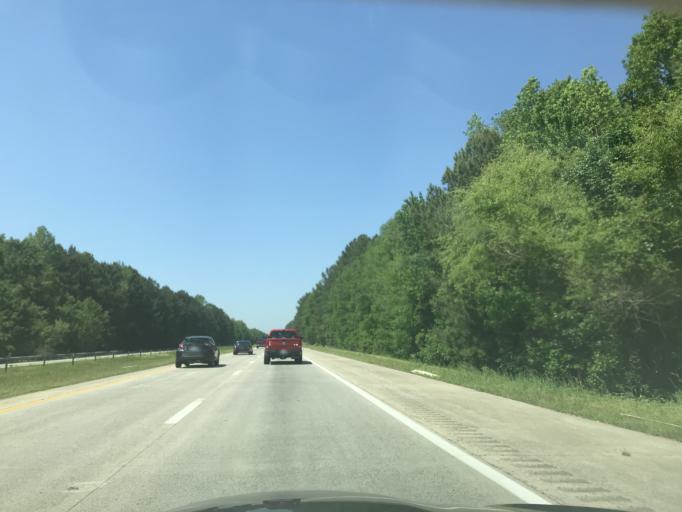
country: US
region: North Carolina
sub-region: Johnston County
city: Benson
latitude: 35.4907
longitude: -78.5523
